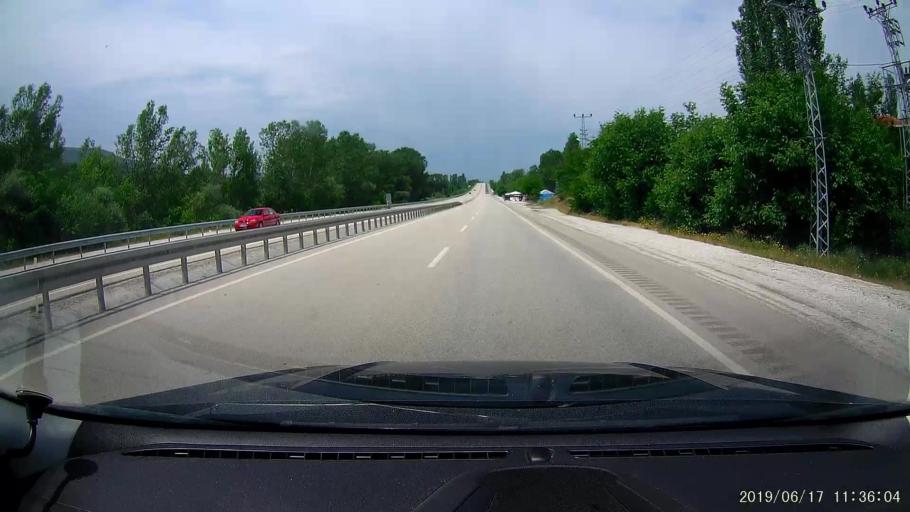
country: TR
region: Cankiri
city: Beloren
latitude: 40.8555
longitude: 33.4560
